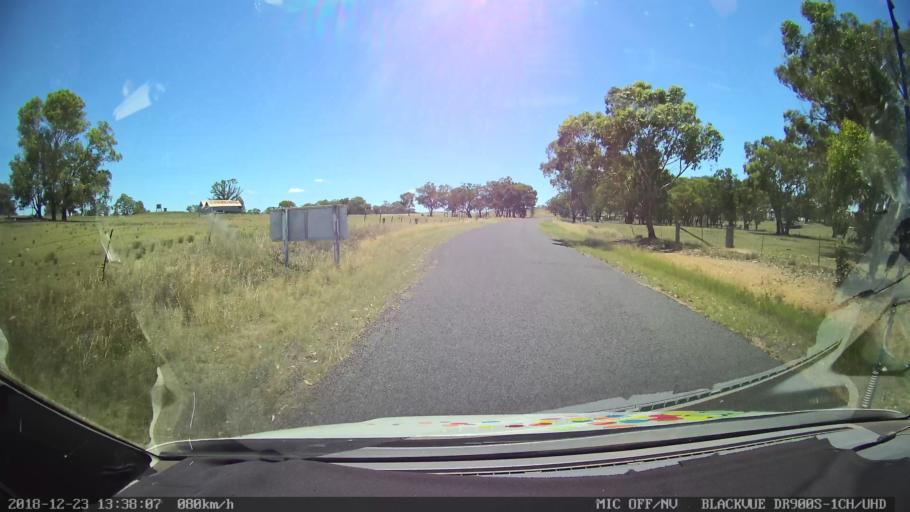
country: AU
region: New South Wales
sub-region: Armidale Dumaresq
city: Armidale
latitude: -30.4516
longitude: 151.2178
